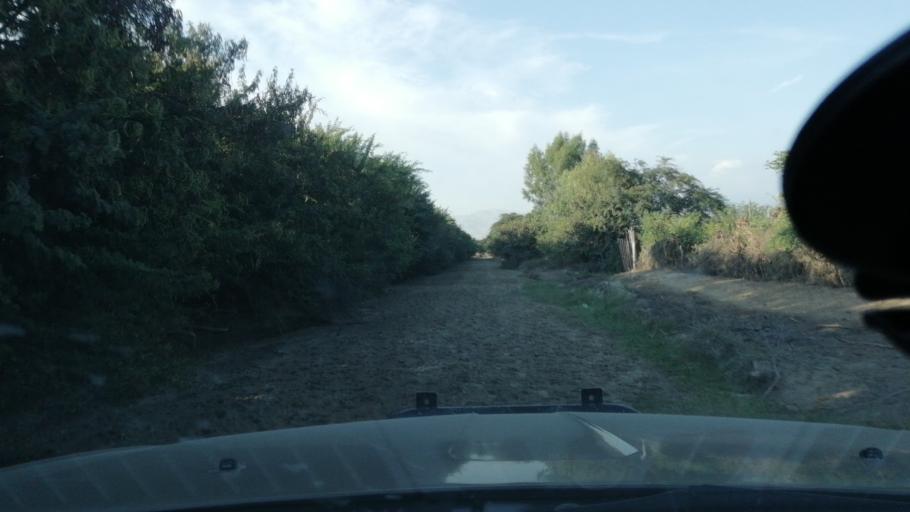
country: PE
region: Ica
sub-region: Provincia de Chincha
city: San Pedro
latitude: -13.3485
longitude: -76.1621
